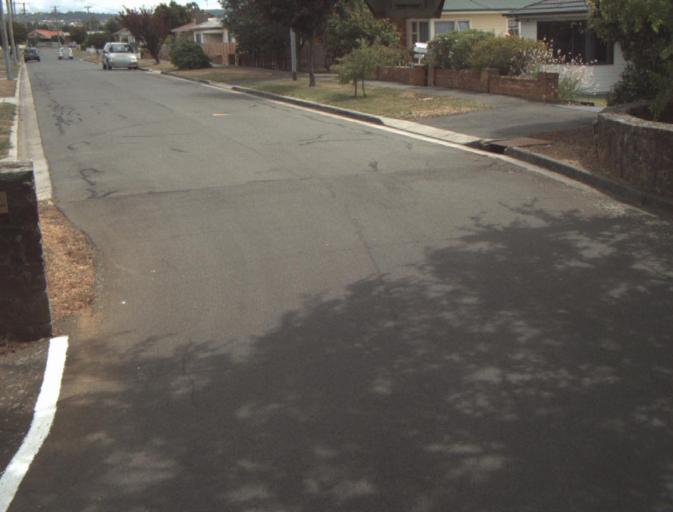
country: AU
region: Tasmania
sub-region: Launceston
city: Newnham
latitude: -41.3986
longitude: 147.1324
